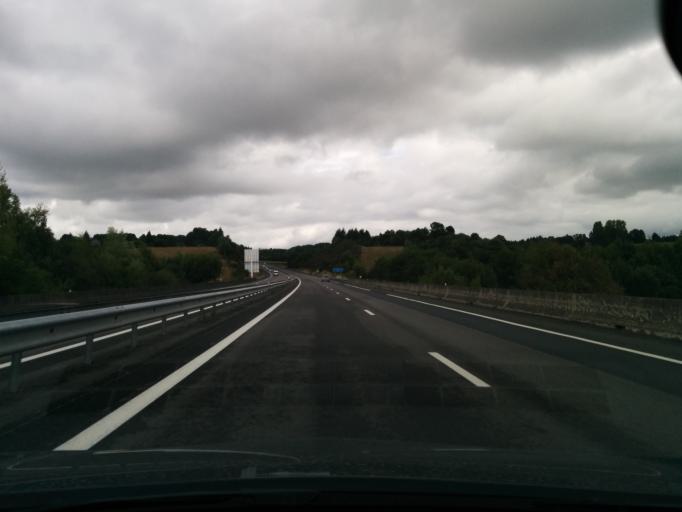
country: FR
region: Limousin
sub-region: Departement de la Correze
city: Vigeois
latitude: 45.3377
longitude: 1.5724
